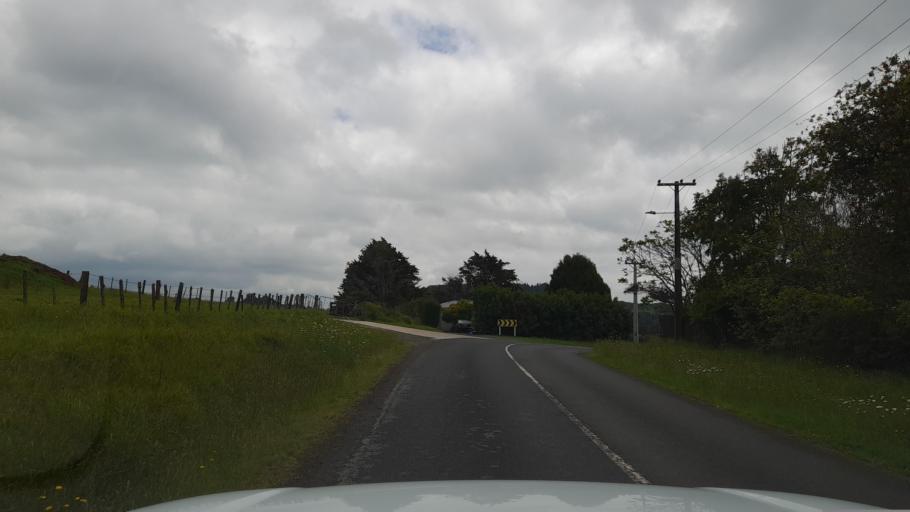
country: NZ
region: Northland
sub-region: Far North District
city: Waimate North
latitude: -35.4062
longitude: 173.7855
